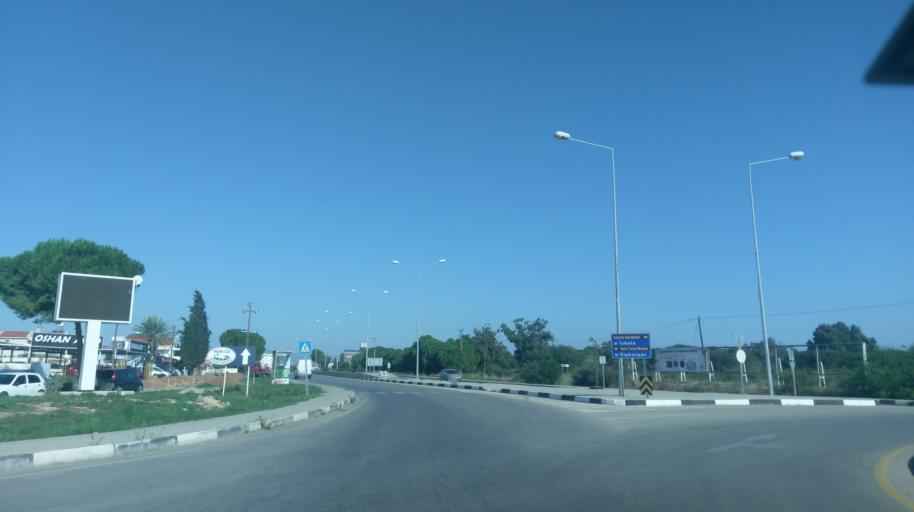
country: CY
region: Ammochostos
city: Famagusta
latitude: 35.1844
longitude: 33.8944
